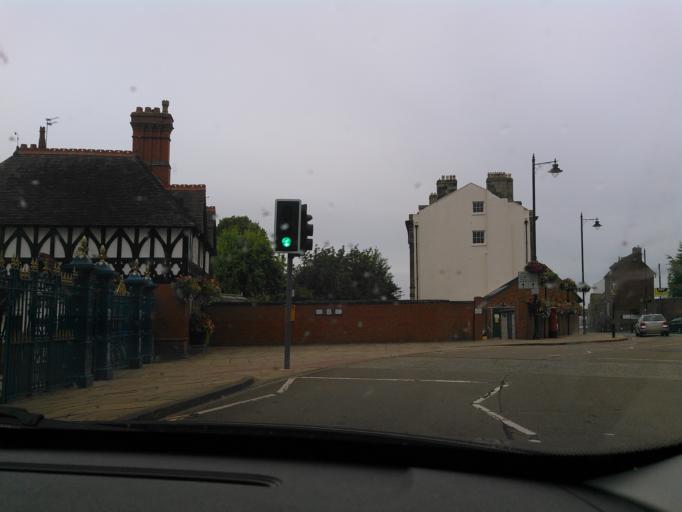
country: GB
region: England
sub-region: Shropshire
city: Shrewsbury
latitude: 52.7073
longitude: -2.7593
